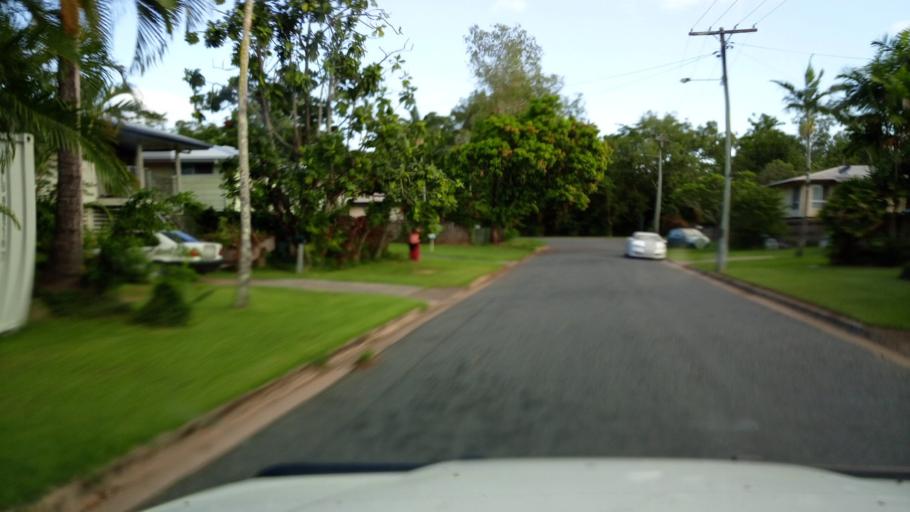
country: AU
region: Queensland
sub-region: Cairns
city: Cairns
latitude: -16.9161
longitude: 145.7562
